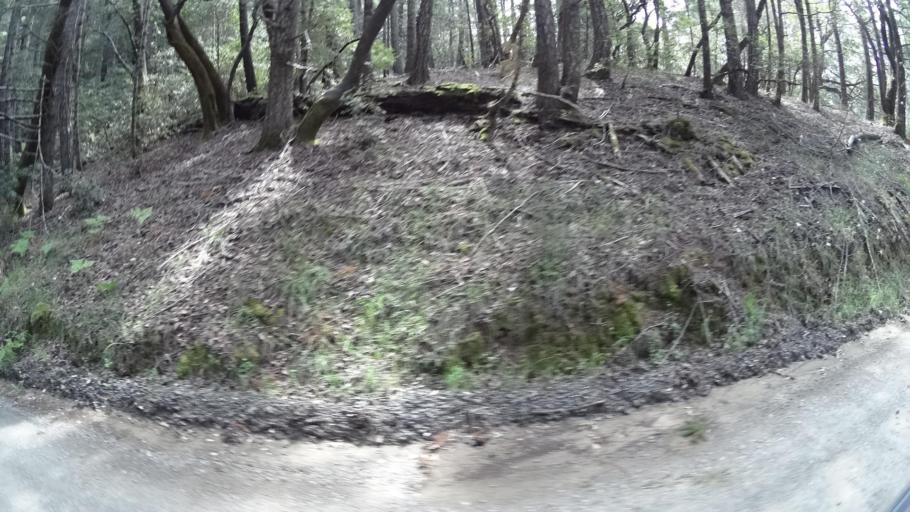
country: US
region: California
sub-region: Humboldt County
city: Redway
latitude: 40.0355
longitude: -123.8393
